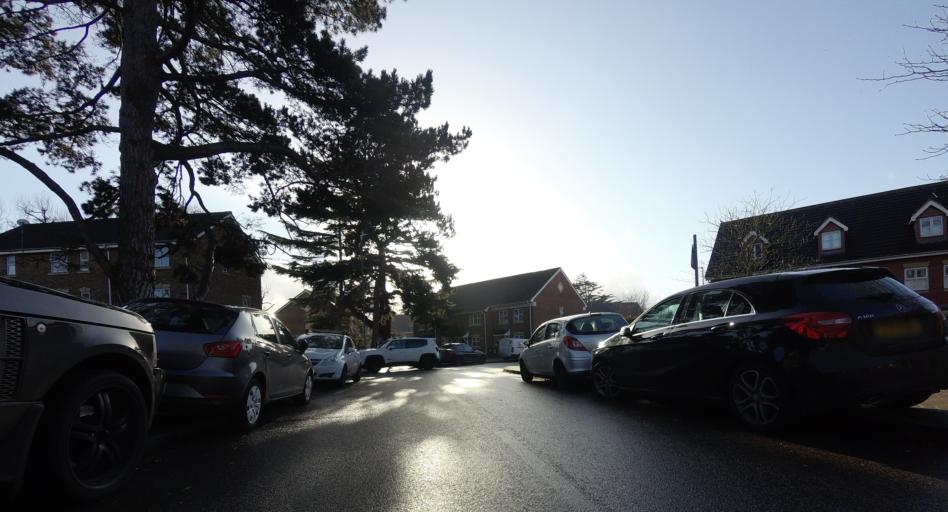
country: GB
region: England
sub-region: Greater London
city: Bexley
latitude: 51.4338
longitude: 0.1776
